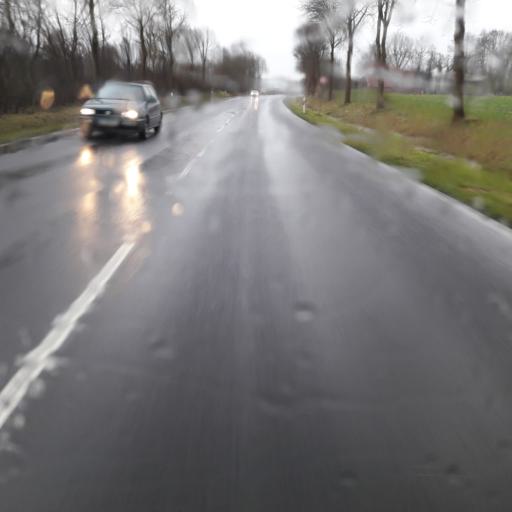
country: DE
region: North Rhine-Westphalia
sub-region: Regierungsbezirk Detmold
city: Petershagen
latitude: 52.3934
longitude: 8.9571
